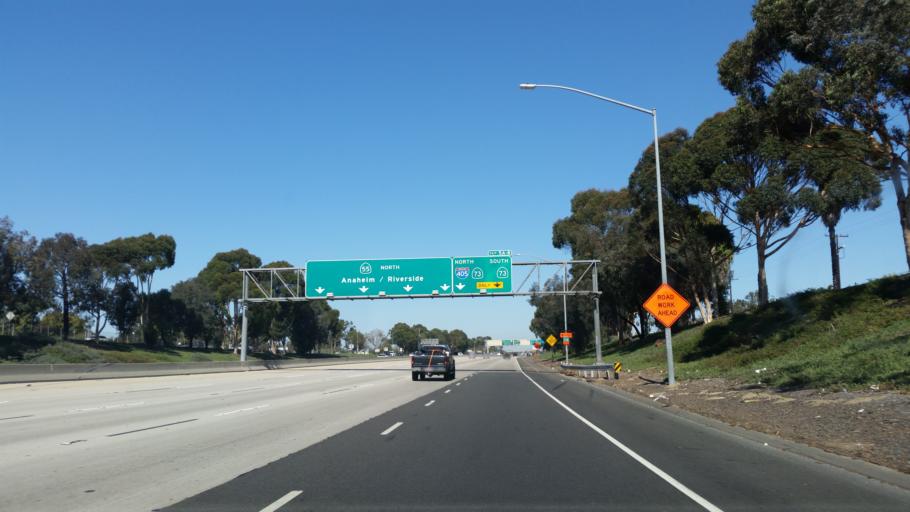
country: US
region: California
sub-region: Orange County
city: Costa Mesa
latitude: 33.6661
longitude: -117.8943
